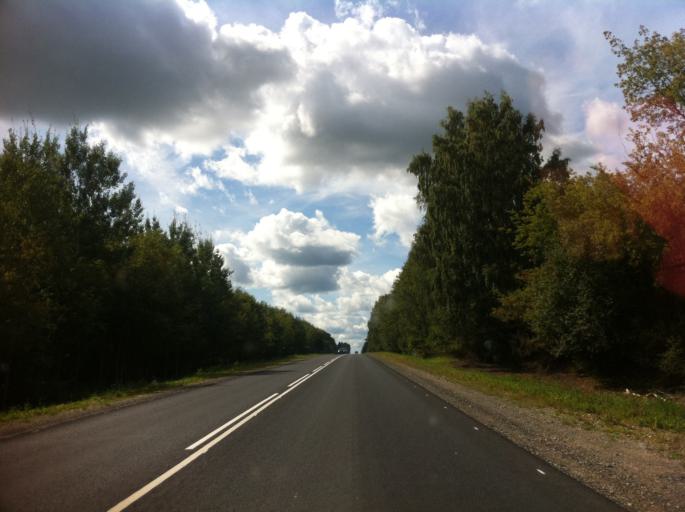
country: RU
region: Pskov
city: Izborsk
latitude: 57.7213
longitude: 27.9371
